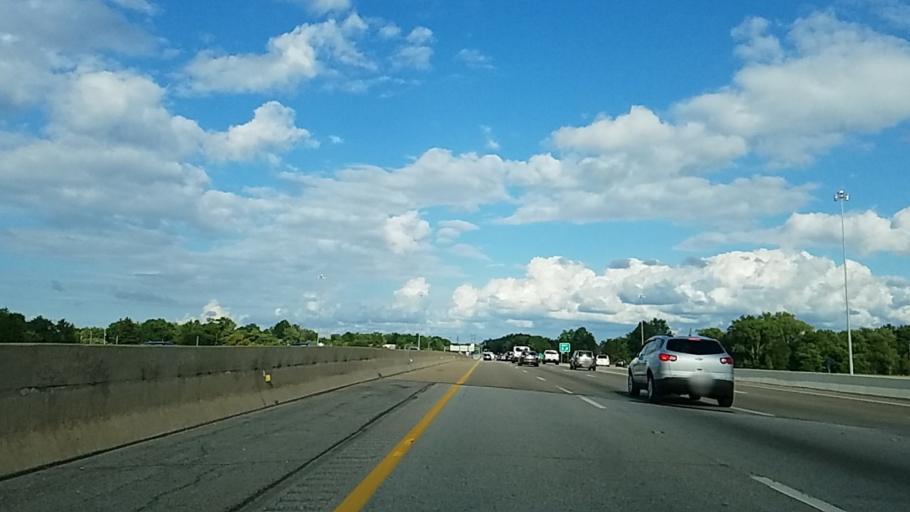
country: US
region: Ohio
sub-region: Lorain County
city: North Ridgeville
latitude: 41.3882
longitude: -81.9735
